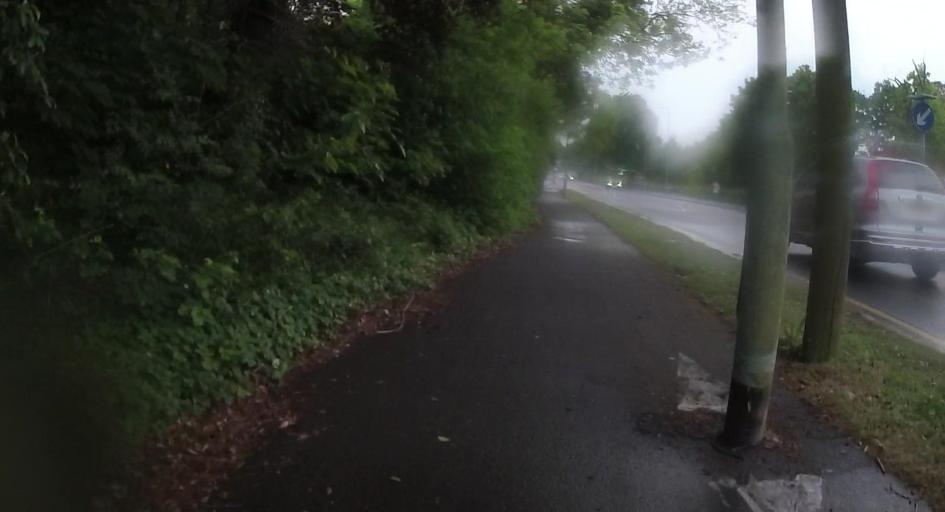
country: GB
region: England
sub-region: Bracknell Forest
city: Bracknell
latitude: 51.4182
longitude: -0.7626
